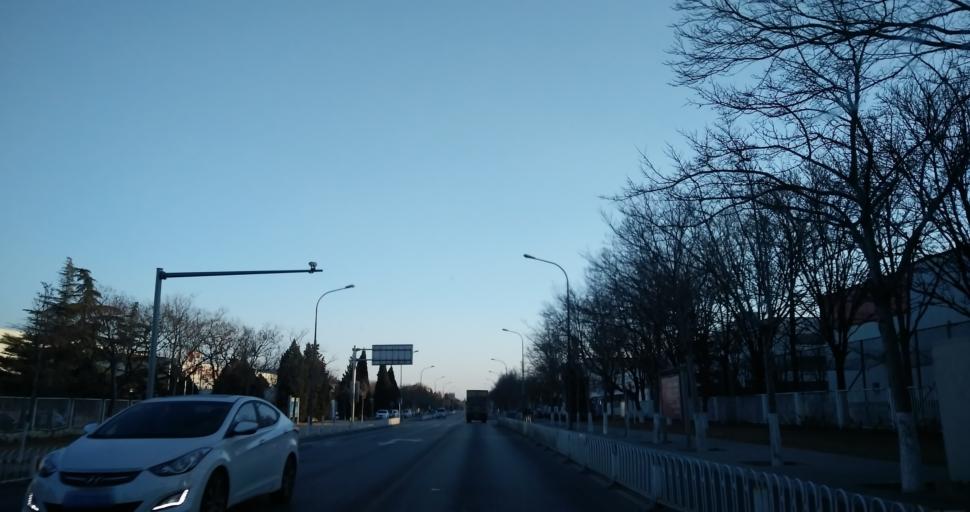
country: CN
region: Beijing
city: Jiugong
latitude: 39.8045
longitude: 116.5031
